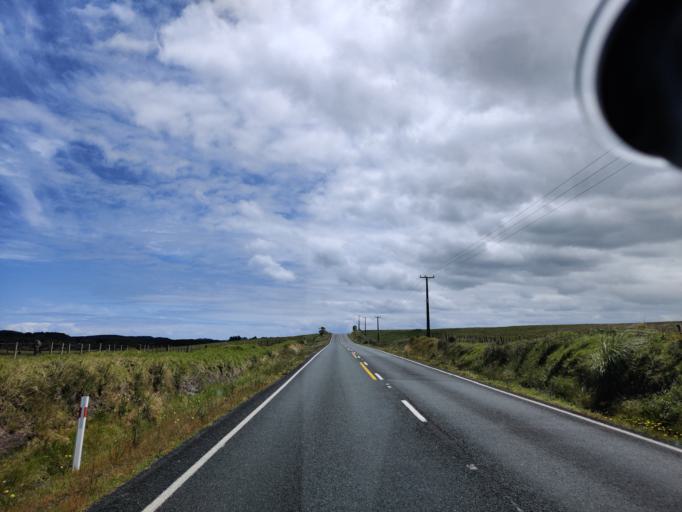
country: NZ
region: Northland
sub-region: Far North District
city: Kaitaia
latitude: -34.6882
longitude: 173.0160
